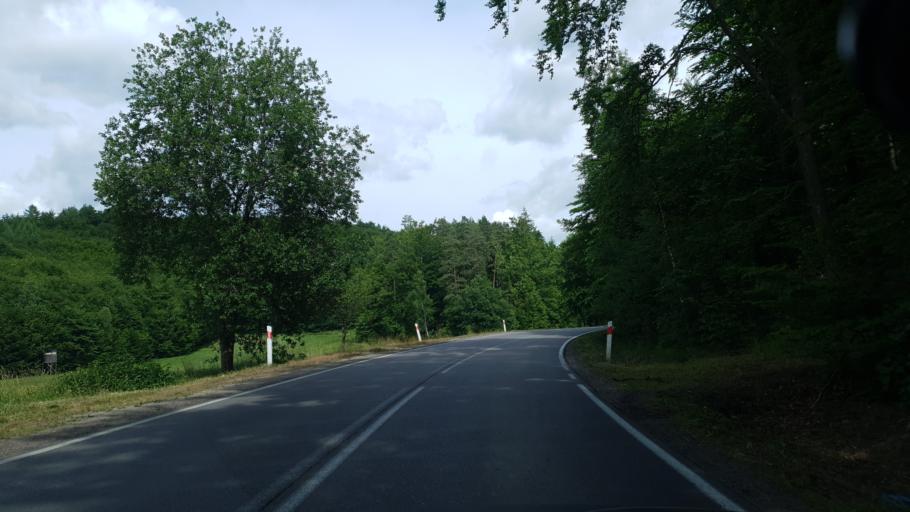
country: PL
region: Pomeranian Voivodeship
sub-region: Powiat kartuski
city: Kartuzy
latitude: 54.3171
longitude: 18.1662
